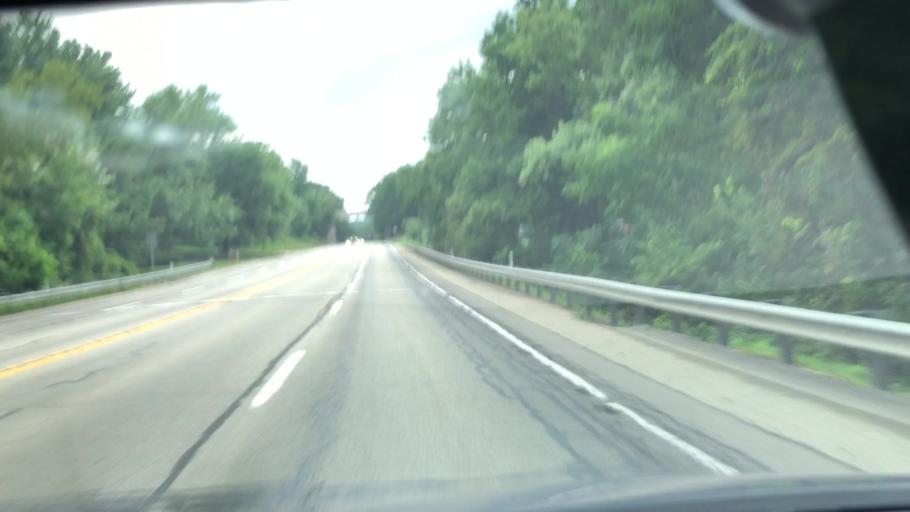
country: US
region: Pennsylvania
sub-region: Allegheny County
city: Upper Saint Clair
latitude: 40.3261
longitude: -80.0784
